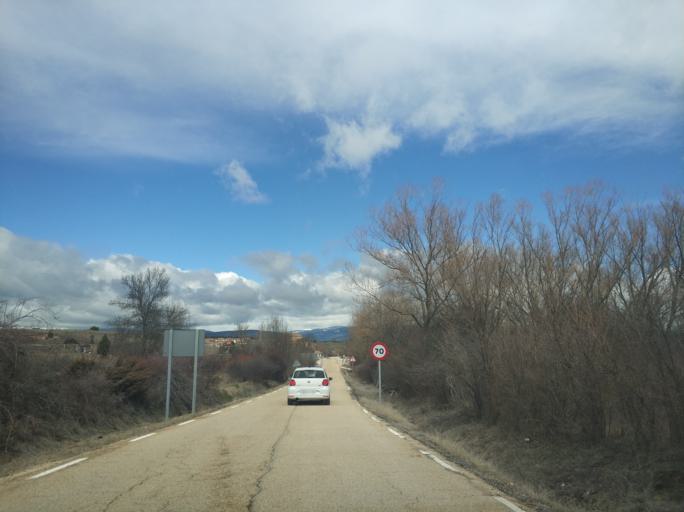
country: ES
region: Castille and Leon
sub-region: Provincia de Soria
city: Abejar
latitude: 41.8002
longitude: -2.7815
